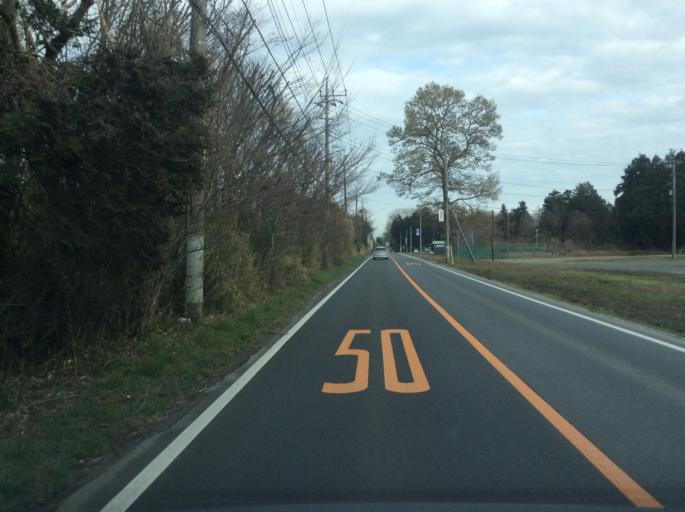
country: JP
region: Ibaraki
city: Tsukuba
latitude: 36.1883
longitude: 140.0236
